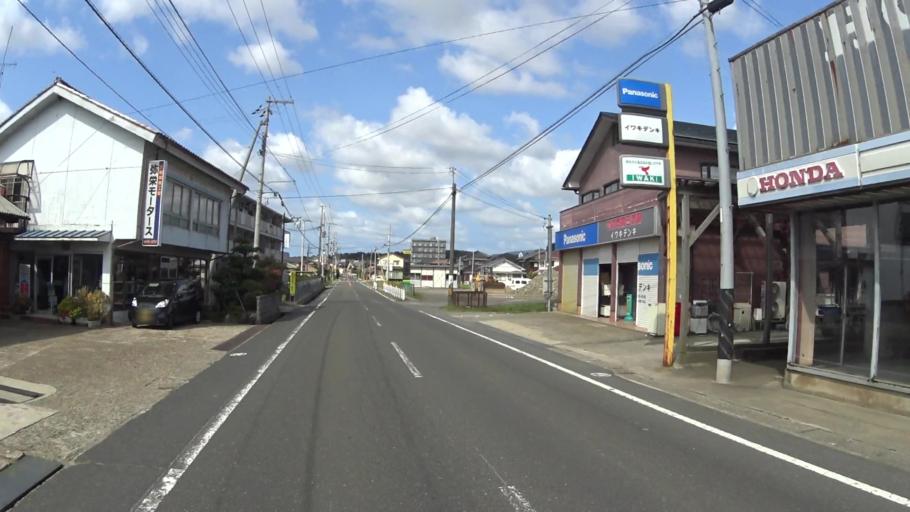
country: JP
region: Kyoto
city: Miyazu
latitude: 35.6523
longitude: 135.0923
